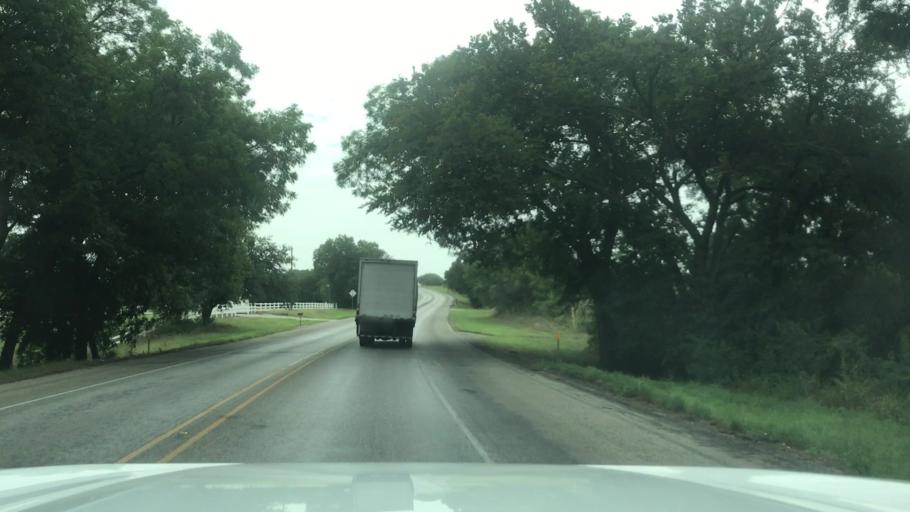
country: US
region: Texas
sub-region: Comanche County
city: De Leon
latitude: 32.1025
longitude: -98.4800
